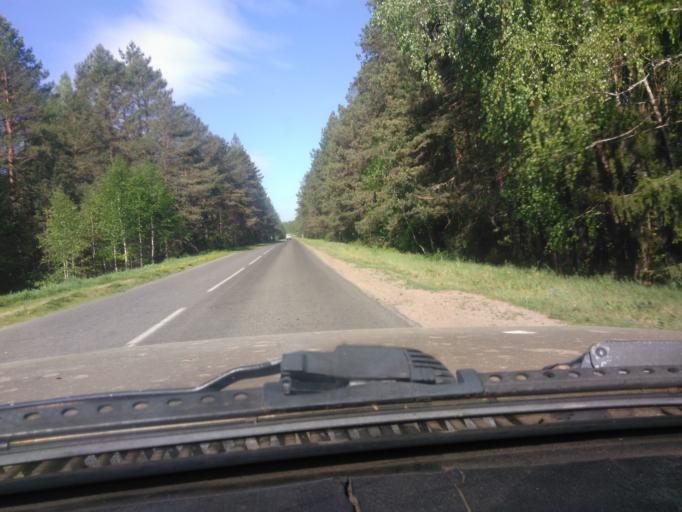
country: BY
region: Mogilev
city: Myazhysyatki
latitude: 53.8120
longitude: 30.1174
